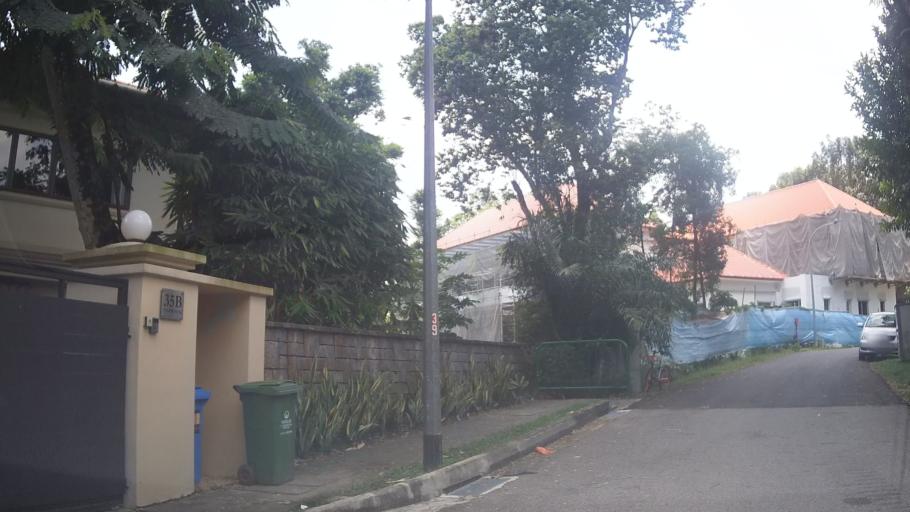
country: SG
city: Singapore
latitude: 1.3416
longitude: 103.7838
